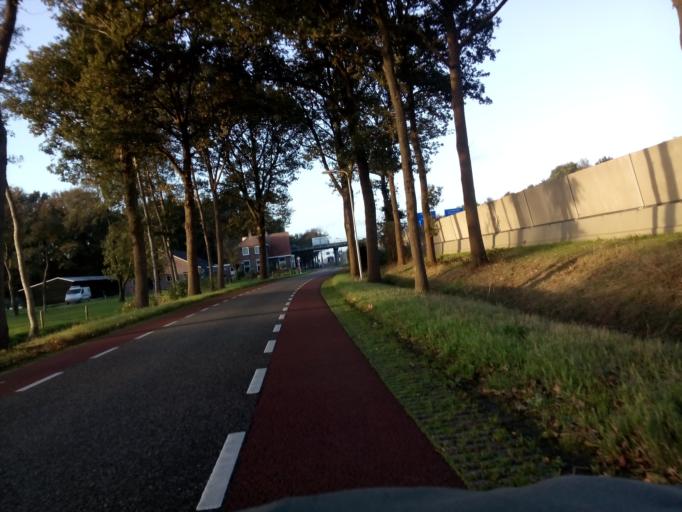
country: NL
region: Overijssel
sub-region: Gemeente Staphorst
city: Staphorst
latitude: 52.6539
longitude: 6.1992
